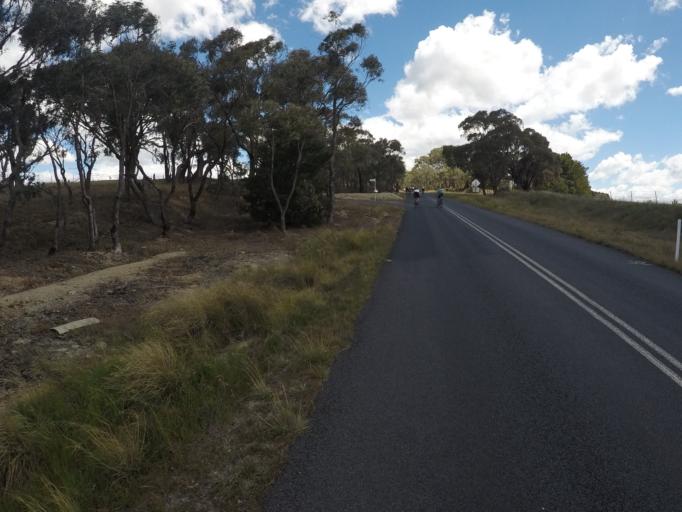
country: AU
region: New South Wales
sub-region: Blayney
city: Blayney
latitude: -33.5798
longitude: 149.3980
